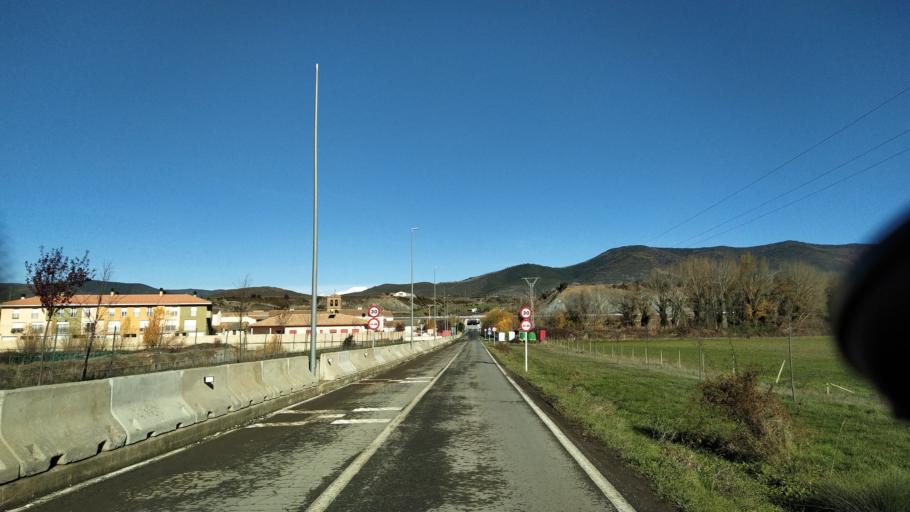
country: ES
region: Aragon
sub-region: Provincia de Huesca
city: Santa Cruz de la Seros
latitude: 42.5586
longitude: -0.7128
